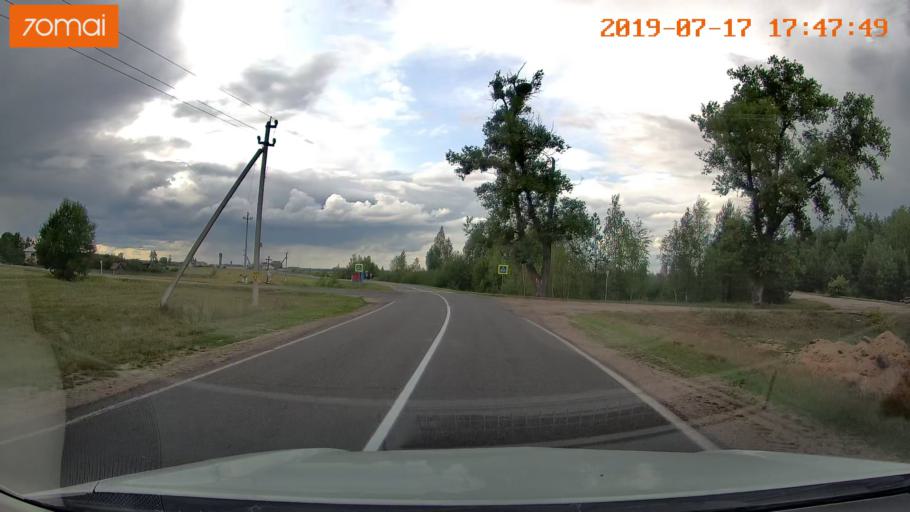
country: BY
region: Mogilev
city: Hlusha
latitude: 53.1156
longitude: 28.8286
